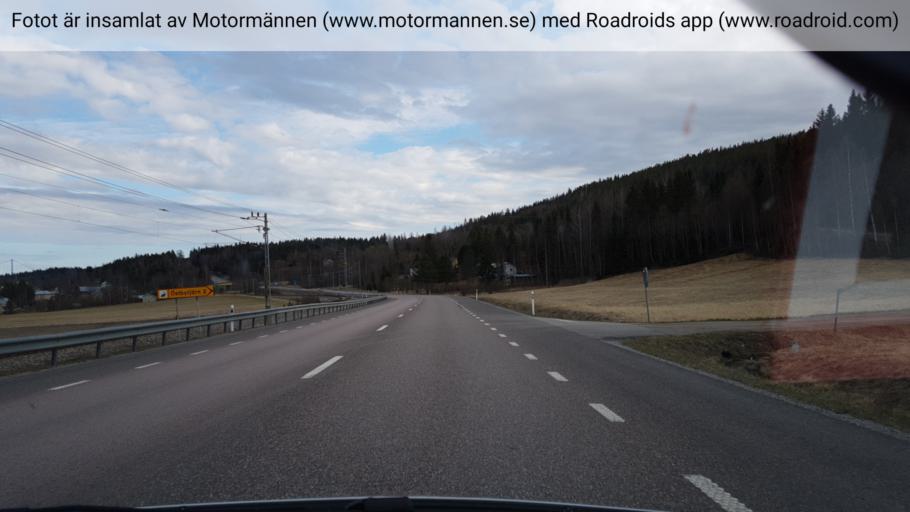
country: SE
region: Vaesternorrland
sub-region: Kramfors Kommun
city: Kramfors
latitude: 62.8227
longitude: 17.8488
